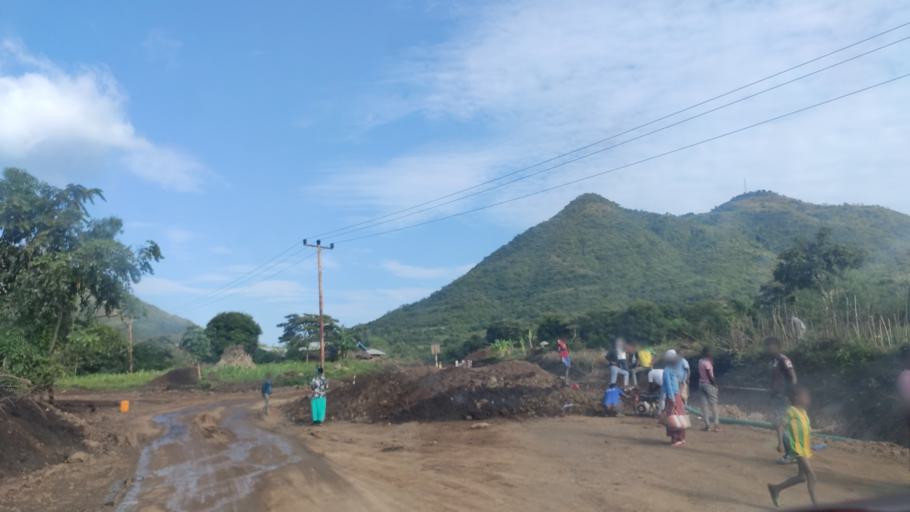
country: ET
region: Southern Nations, Nationalities, and People's Region
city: Arba Minch'
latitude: 6.4260
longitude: 37.3338
